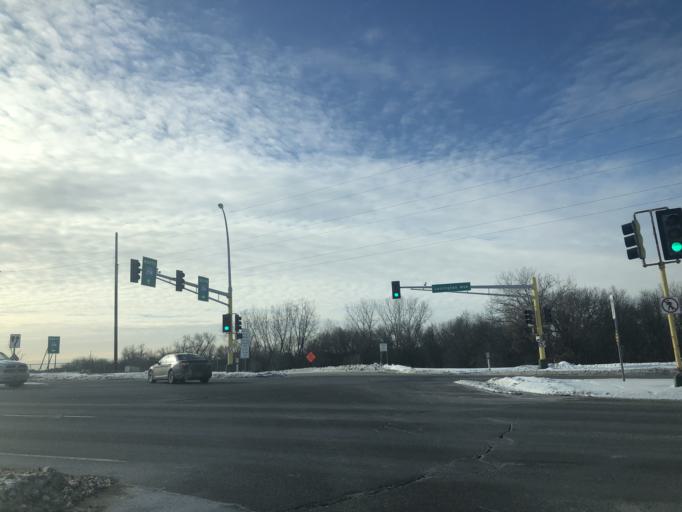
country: US
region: Minnesota
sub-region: Anoka County
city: Circle Pines
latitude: 45.1605
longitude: -93.1630
